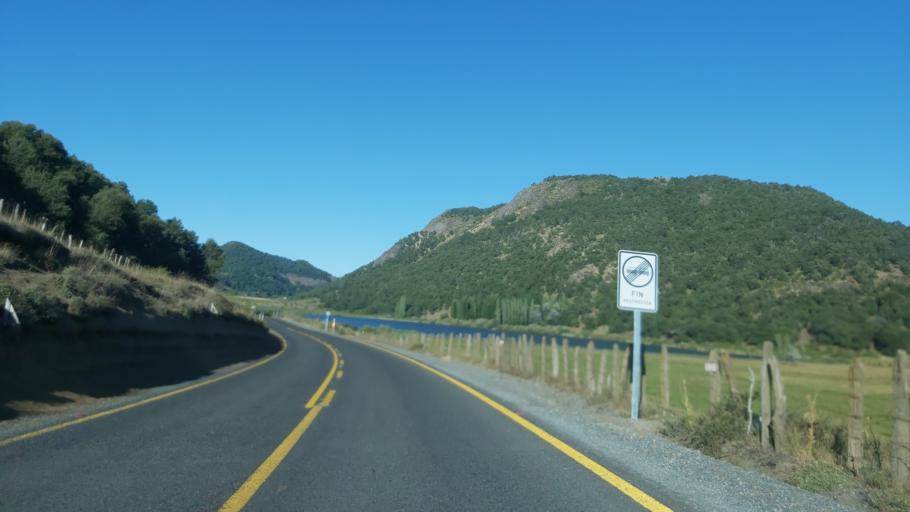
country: AR
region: Neuquen
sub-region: Departamento de Loncopue
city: Loncopue
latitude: -38.4431
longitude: -71.3406
